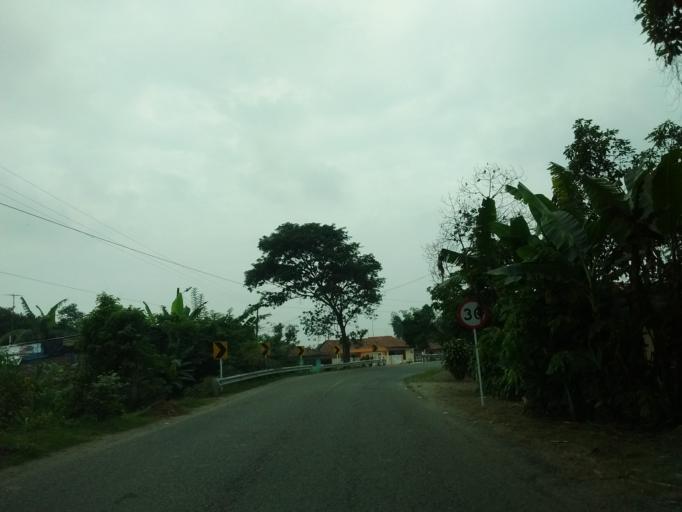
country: CO
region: Cauca
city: Puerto Tejada
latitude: 3.2194
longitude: -76.3915
